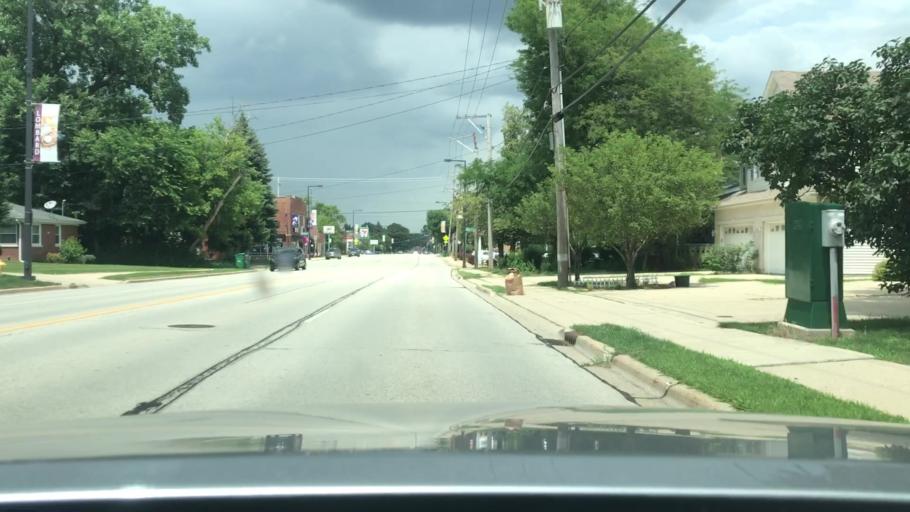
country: US
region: Illinois
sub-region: DuPage County
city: Villa Park
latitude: 41.8805
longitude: -87.9935
